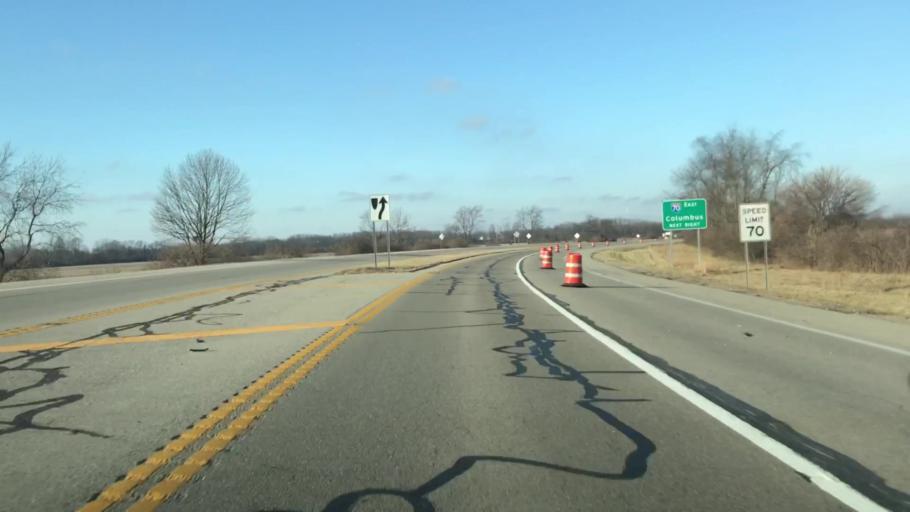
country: US
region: Ohio
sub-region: Clark County
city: Springfield
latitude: 39.8840
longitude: -83.8537
